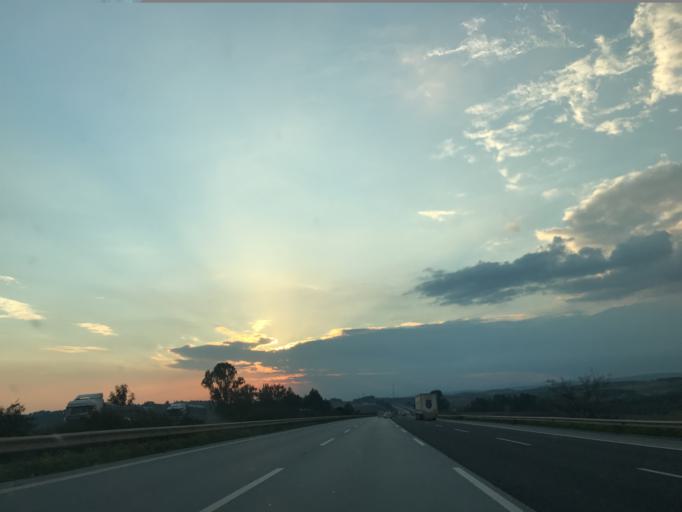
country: TR
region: Mersin
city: Yenice
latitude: 37.0208
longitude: 35.0338
